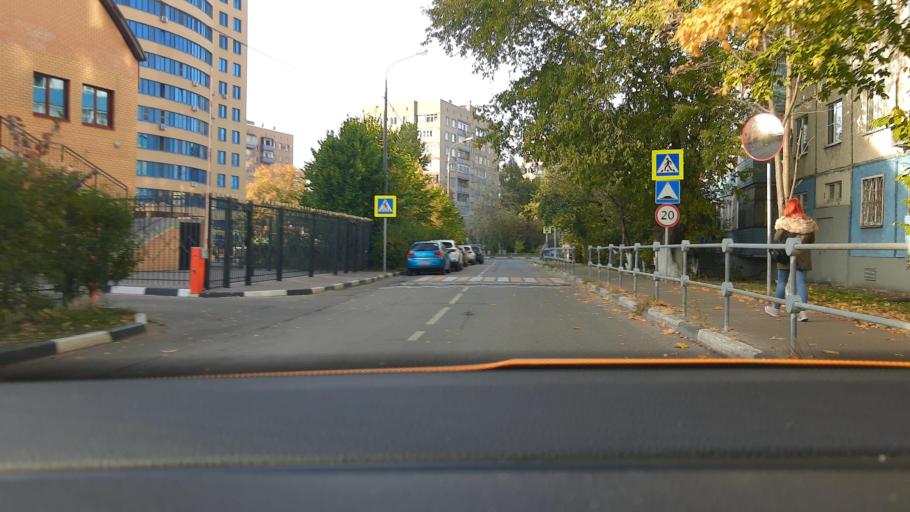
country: RU
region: Moskovskaya
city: Reutov
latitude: 55.7597
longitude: 37.8492
